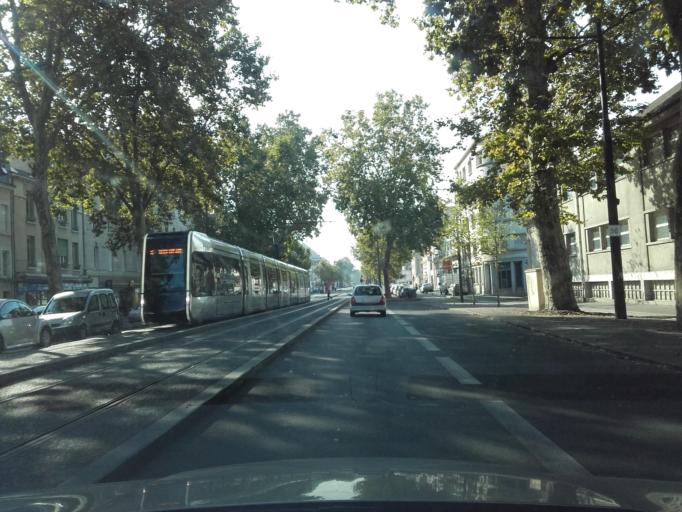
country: FR
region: Centre
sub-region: Departement d'Indre-et-Loire
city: Tours
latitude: 47.3793
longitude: 0.6932
